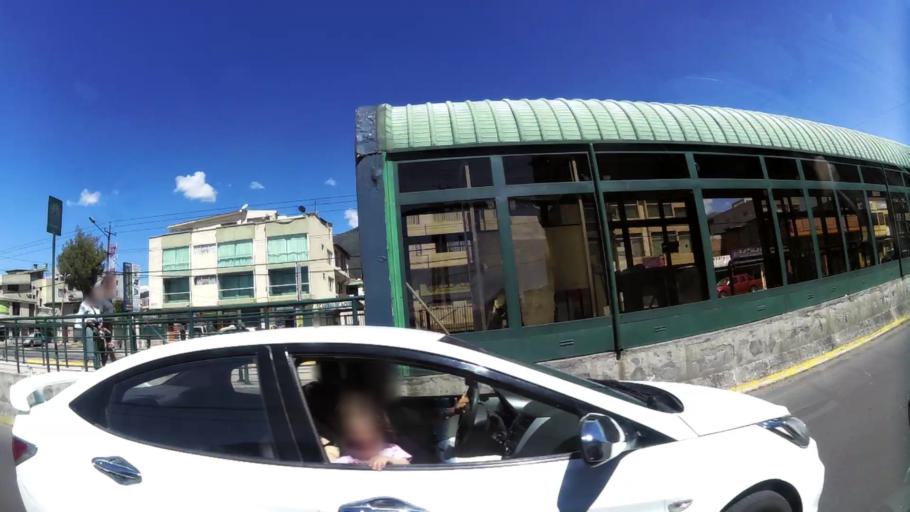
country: EC
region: Pichincha
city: Quito
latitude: -0.1533
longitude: -78.4895
